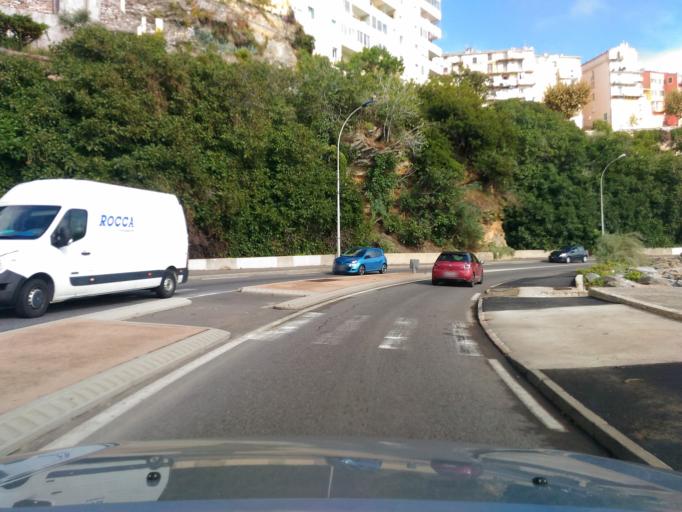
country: FR
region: Corsica
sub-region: Departement de la Haute-Corse
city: Bastia
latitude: 42.6897
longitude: 9.4476
